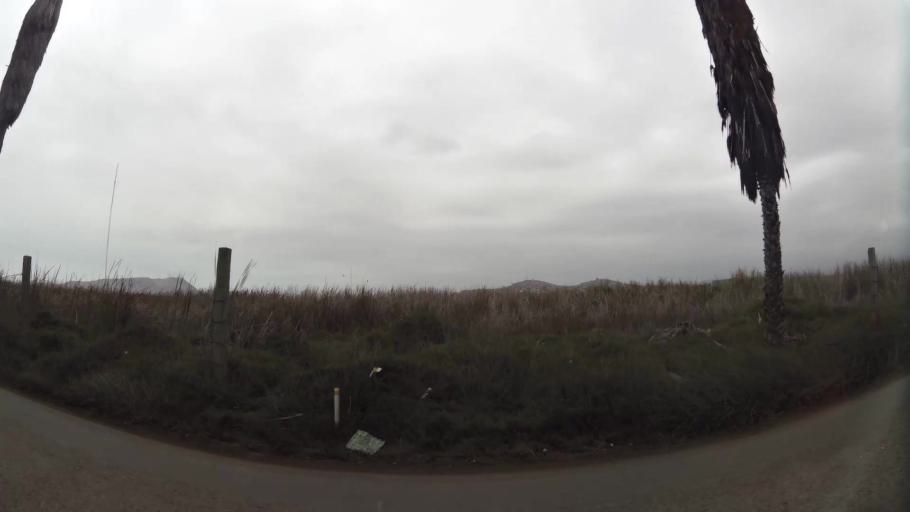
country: PE
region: Lima
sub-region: Lima
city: Surco
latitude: -12.2124
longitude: -76.9913
